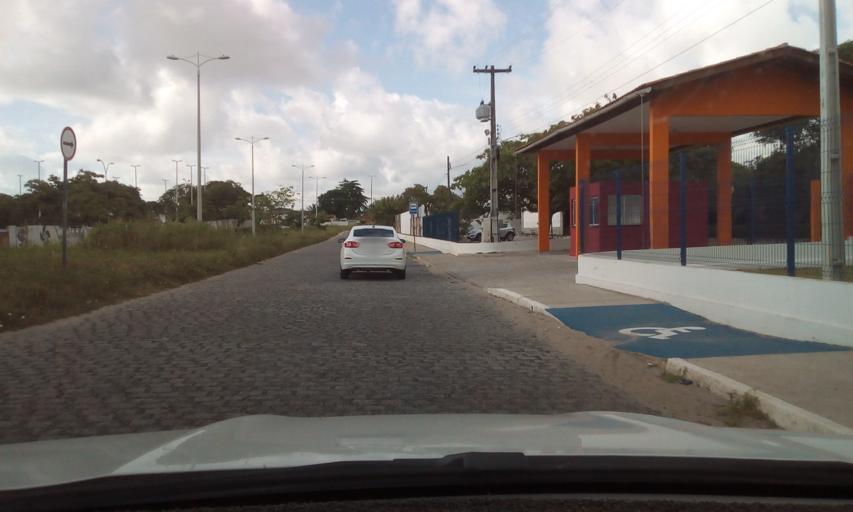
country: BR
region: Paraiba
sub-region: Joao Pessoa
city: Joao Pessoa
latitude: -7.1664
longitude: -34.8283
